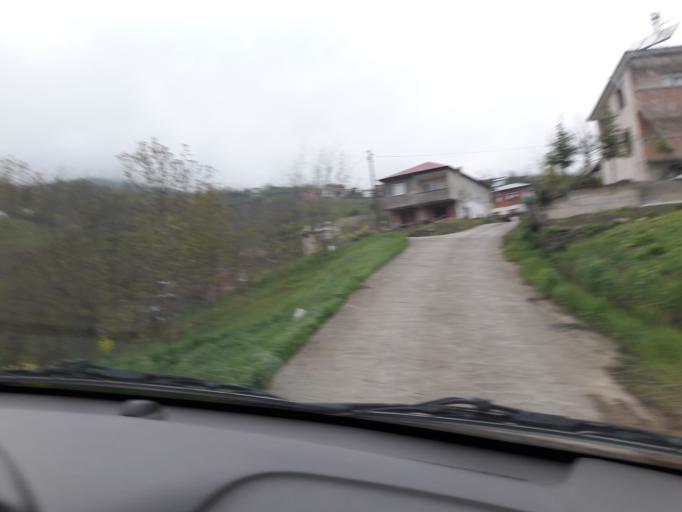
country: TR
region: Trabzon
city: Duzkoy
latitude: 40.9289
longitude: 39.4813
